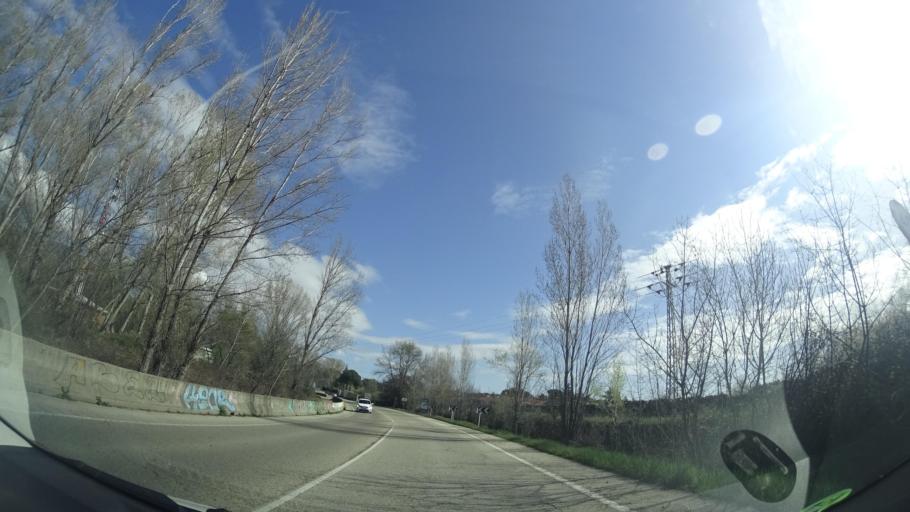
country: ES
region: Madrid
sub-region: Provincia de Madrid
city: Miraflores de la Sierra
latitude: 40.7433
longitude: -3.7850
